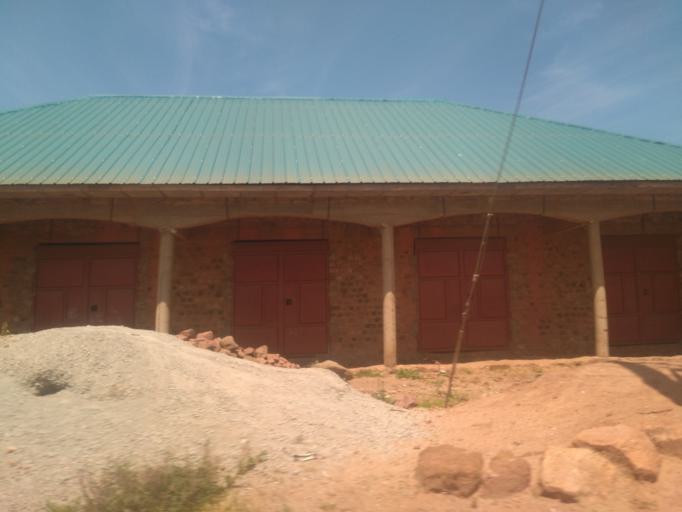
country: UG
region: Central Region
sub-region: Wakiso District
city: Entebbe
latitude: 0.0344
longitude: 32.4356
